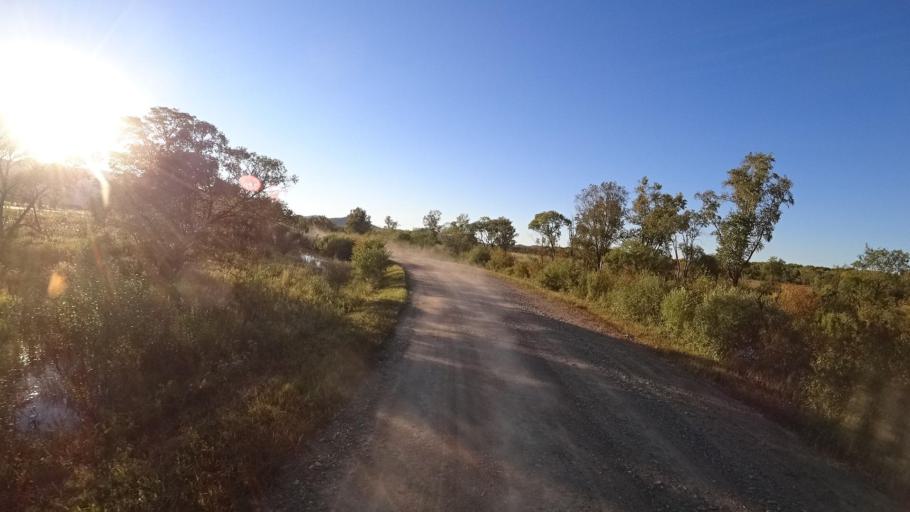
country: RU
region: Primorskiy
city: Kirovskiy
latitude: 44.8142
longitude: 133.6148
